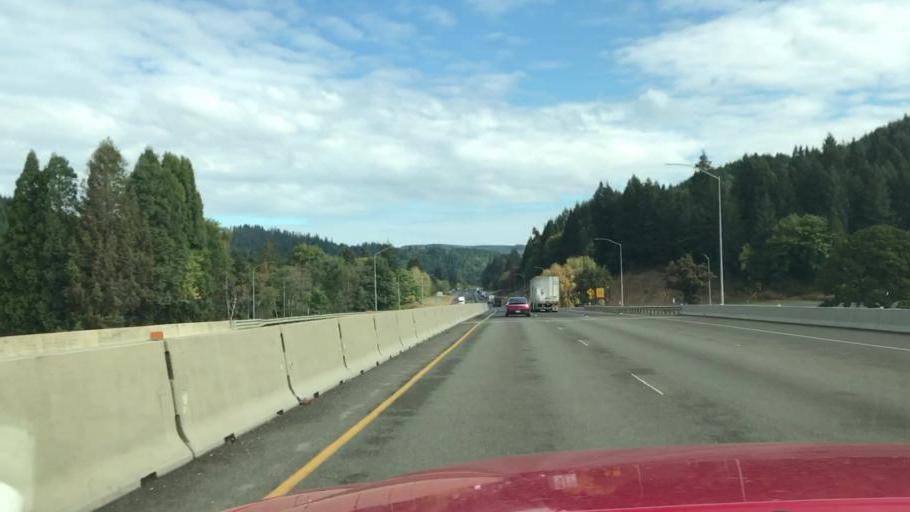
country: US
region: Oregon
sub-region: Douglas County
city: Drain
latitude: 43.7214
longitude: -123.2087
